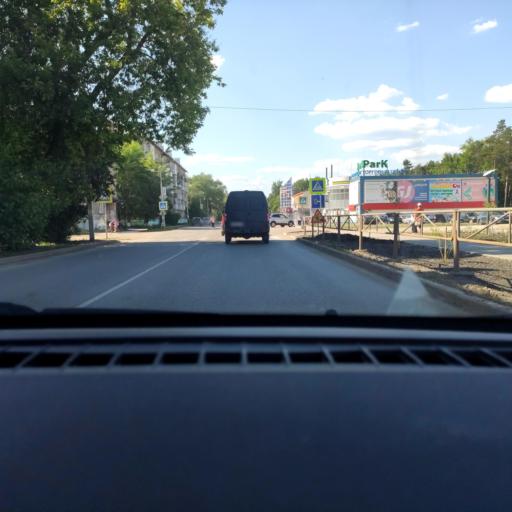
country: RU
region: Perm
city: Krasnokamsk
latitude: 58.0817
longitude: 55.7577
